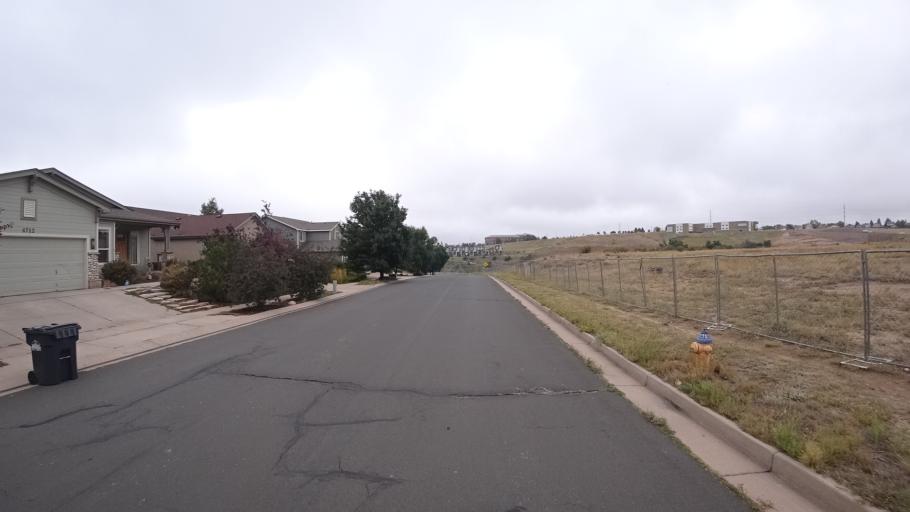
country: US
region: Colorado
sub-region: El Paso County
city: Black Forest
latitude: 38.9357
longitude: -104.7448
